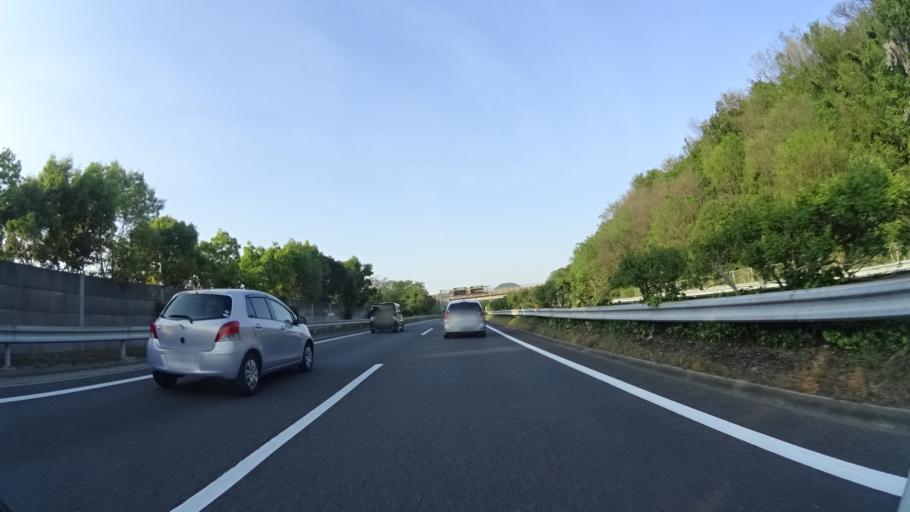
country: JP
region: Kagawa
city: Sakaidecho
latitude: 34.2786
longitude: 133.8390
